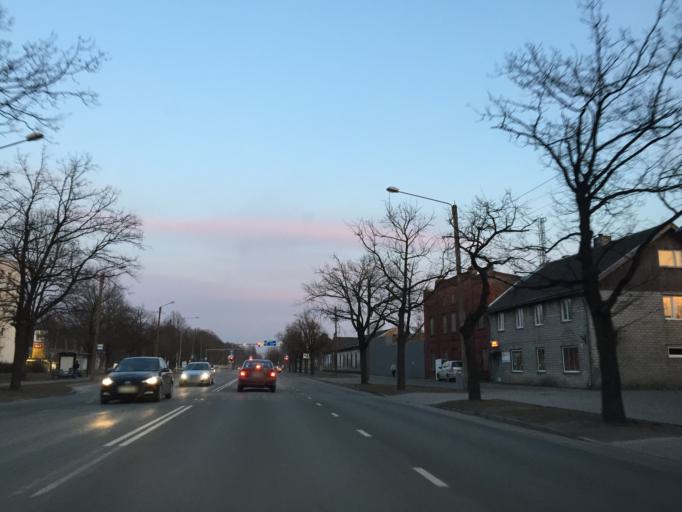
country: EE
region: Paernumaa
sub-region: Paernu linn
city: Parnu
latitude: 58.3788
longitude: 24.5289
